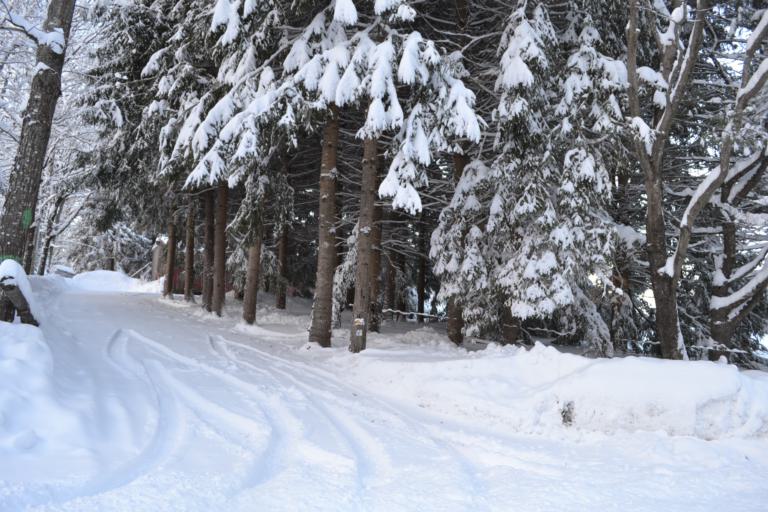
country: US
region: New Hampshire
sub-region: Carroll County
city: Ossipee
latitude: 43.6552
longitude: -71.1519
